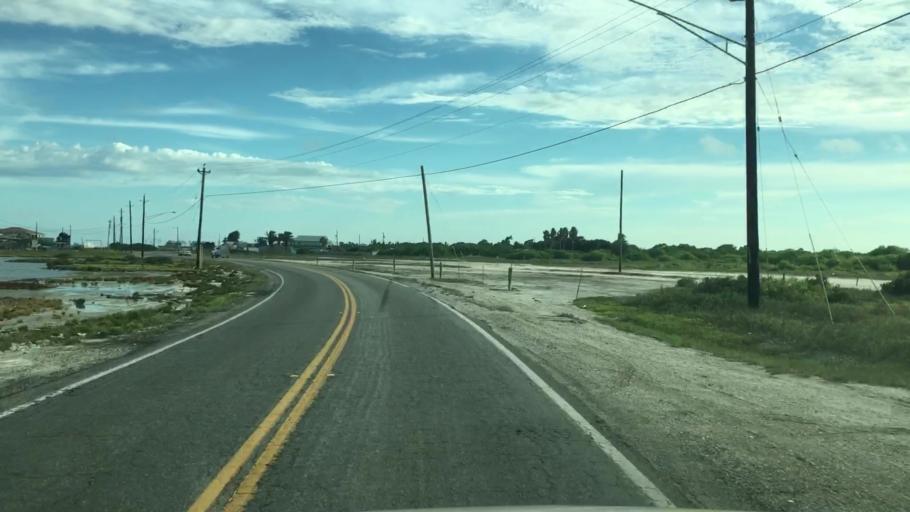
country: US
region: Texas
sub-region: Nueces County
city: Corpus Christi
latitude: 27.6393
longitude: -97.2873
